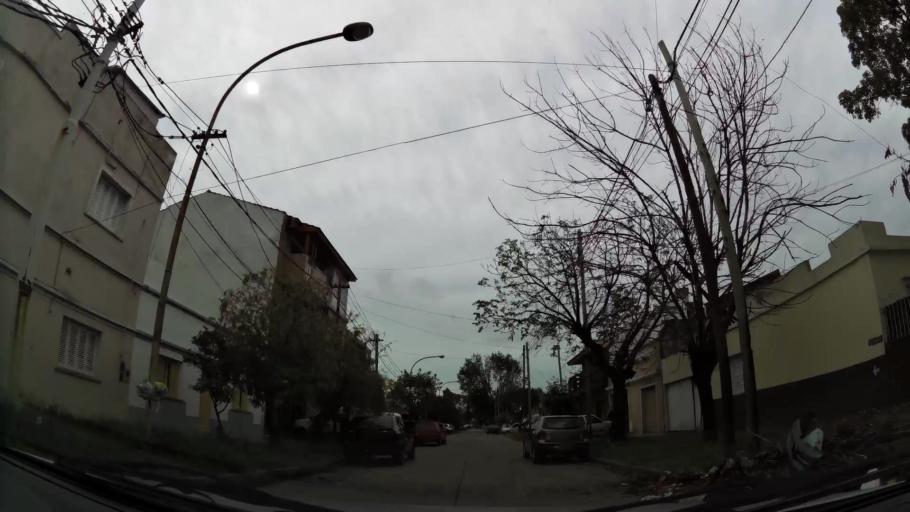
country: AR
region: Buenos Aires
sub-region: Partido de Lanus
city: Lanus
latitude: -34.6973
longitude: -58.3841
